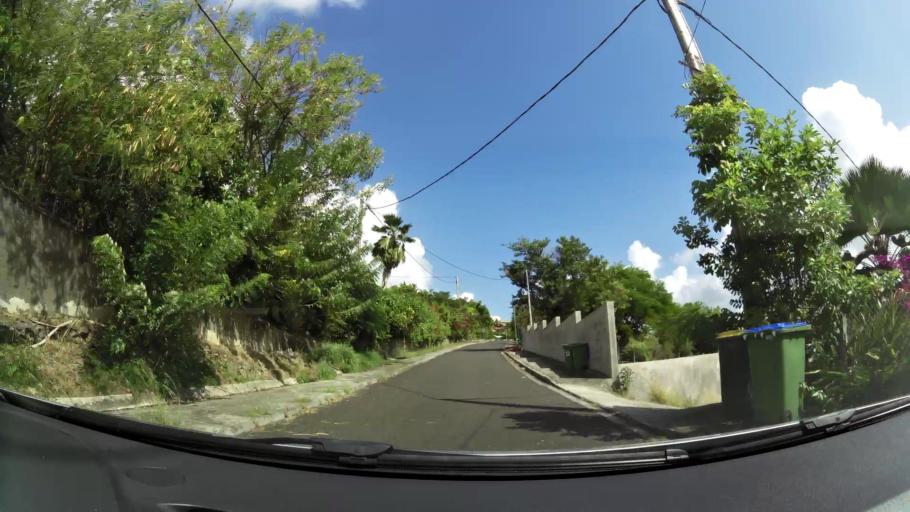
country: MQ
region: Martinique
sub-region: Martinique
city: Fort-de-France
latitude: 14.6349
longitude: -61.1277
